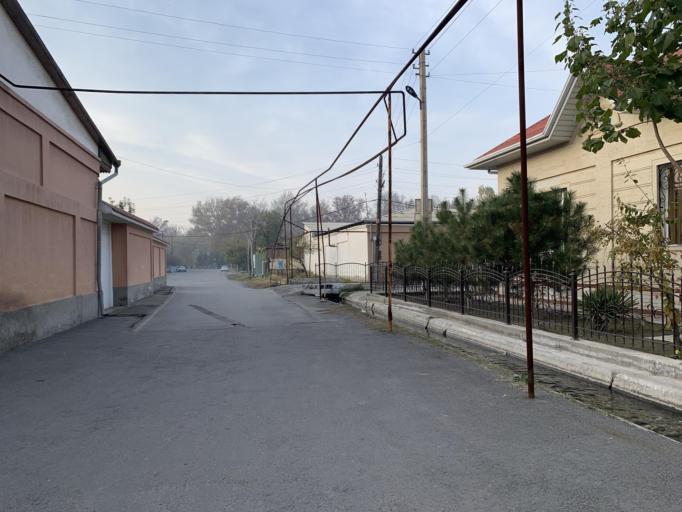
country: UZ
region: Fergana
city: Qo`qon
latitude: 40.5425
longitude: 70.9267
